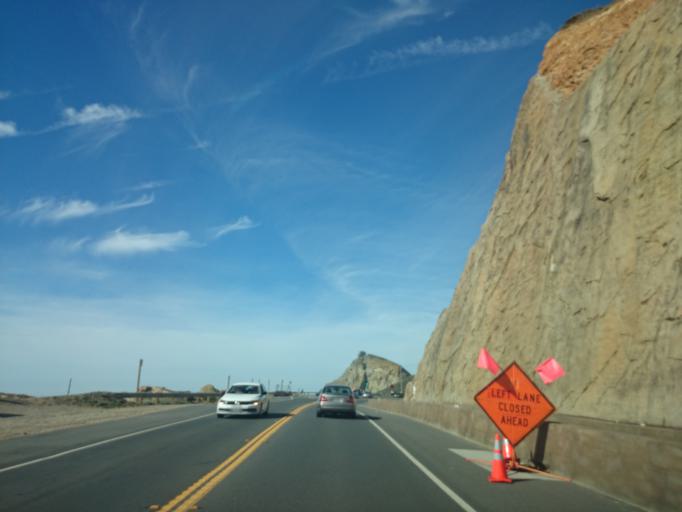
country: US
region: California
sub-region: San Mateo County
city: Montara
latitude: 37.5692
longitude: -122.5150
